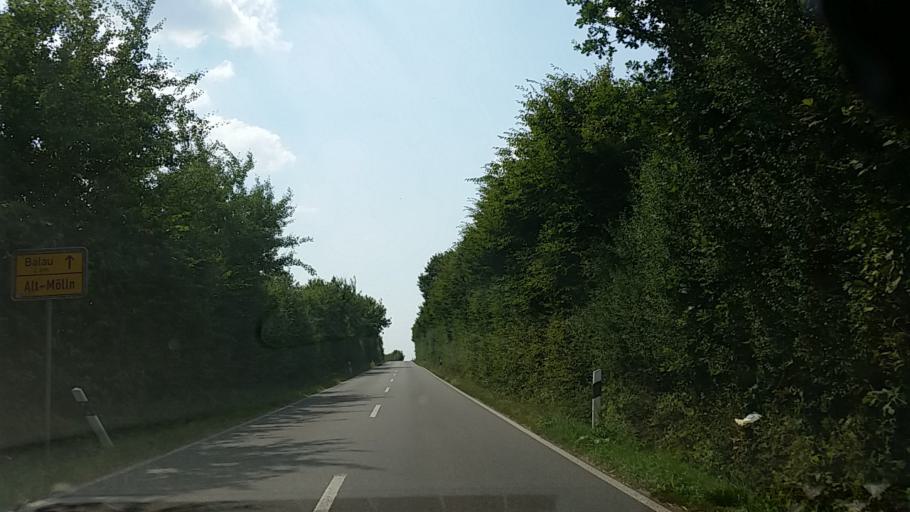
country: DE
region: Schleswig-Holstein
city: Alt Molln
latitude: 53.6189
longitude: 10.6507
